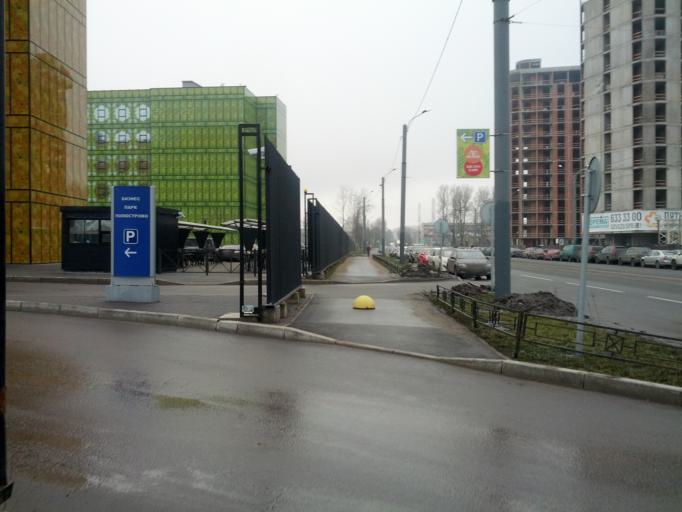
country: RU
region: Leningrad
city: Kalininskiy
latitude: 59.9619
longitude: 30.4044
